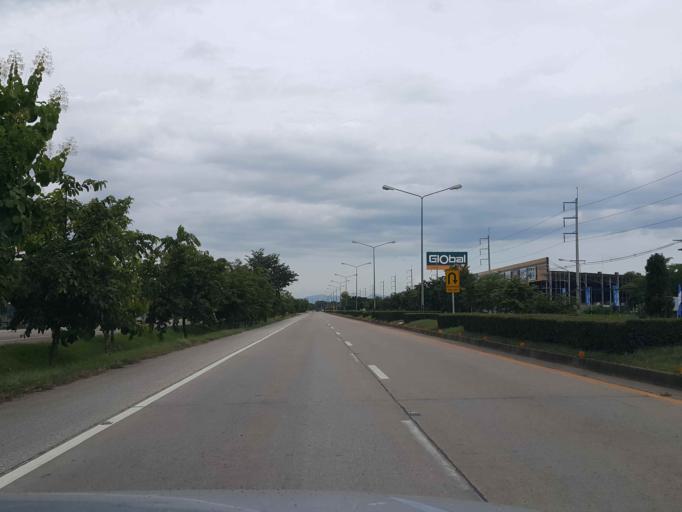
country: TH
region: Lampang
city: Lampang
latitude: 18.2837
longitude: 99.4495
